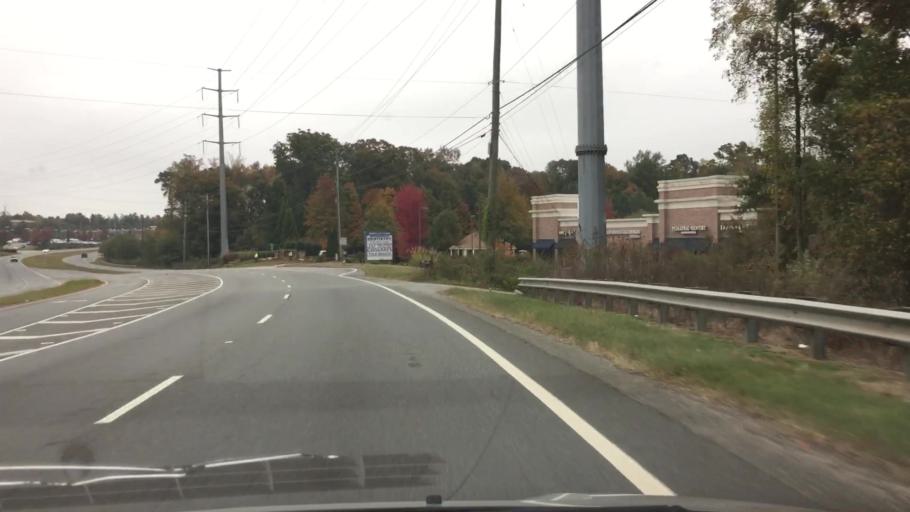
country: US
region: Georgia
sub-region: Fulton County
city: Milton
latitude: 34.1350
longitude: -84.2462
